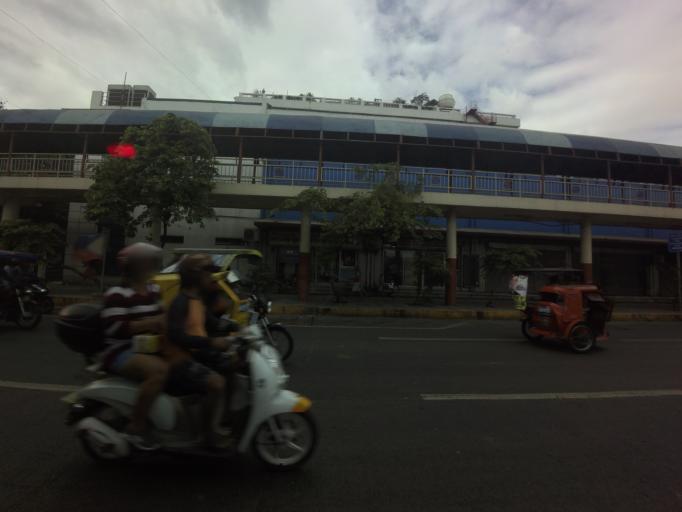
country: PH
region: Calabarzon
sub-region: Province of Rizal
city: Pateros
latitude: 14.5589
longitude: 121.0809
